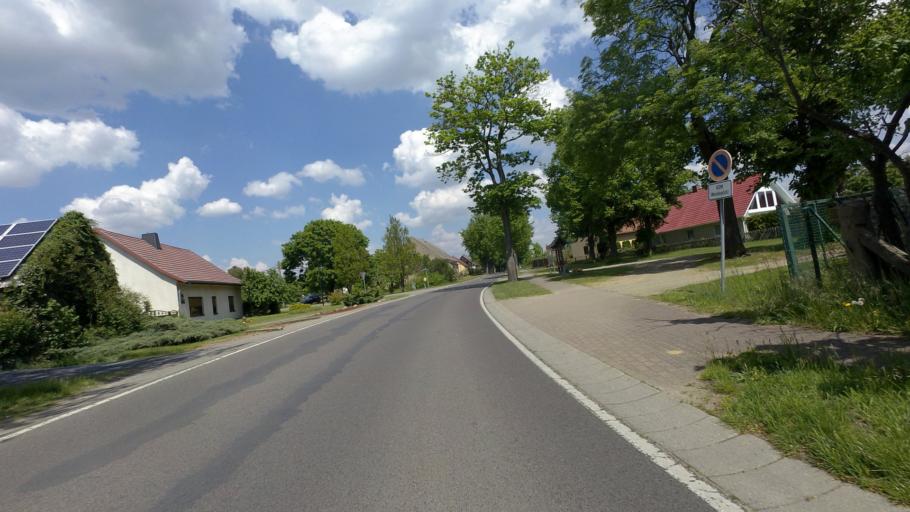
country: DE
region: Brandenburg
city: Straupitz
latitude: 51.9326
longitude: 14.1680
